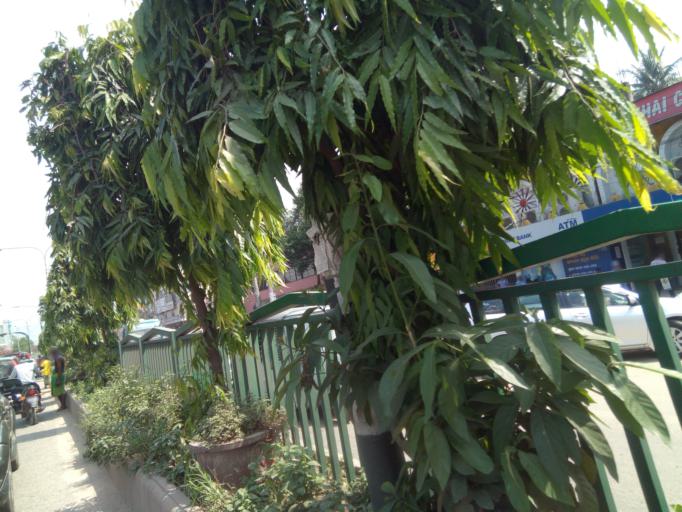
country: BD
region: Dhaka
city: Azimpur
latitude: 23.7592
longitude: 90.3736
